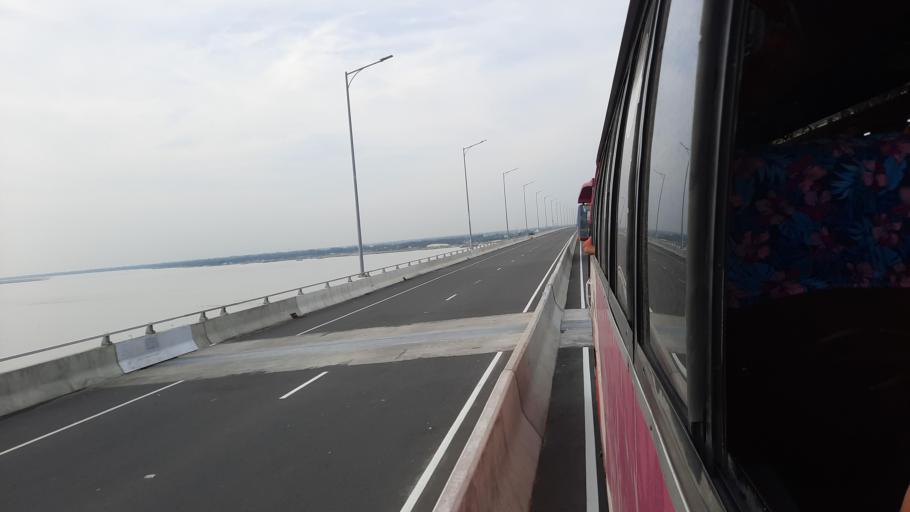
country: BD
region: Dhaka
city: Char Bhadrasan
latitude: 23.4546
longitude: 90.2619
